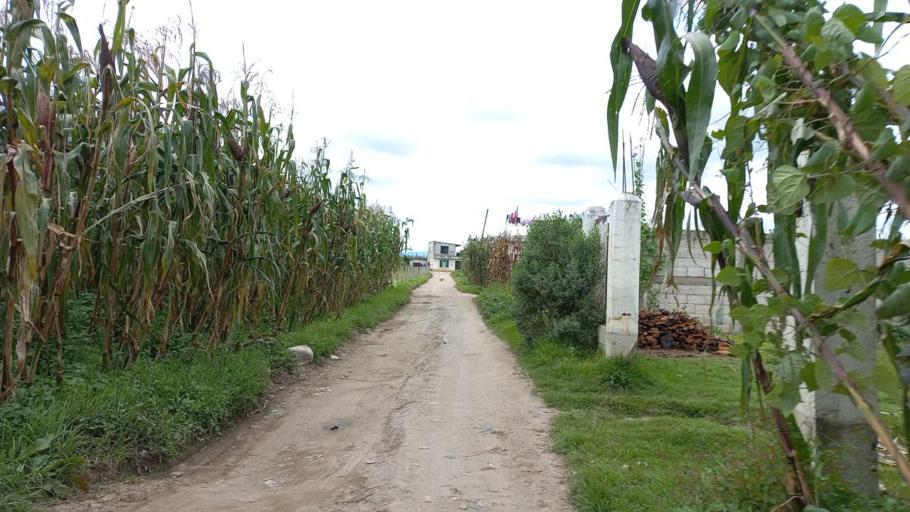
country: GT
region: Totonicapan
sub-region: Municipio de San Andres Xecul
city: San Andres Xecul
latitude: 14.8884
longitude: -91.4699
